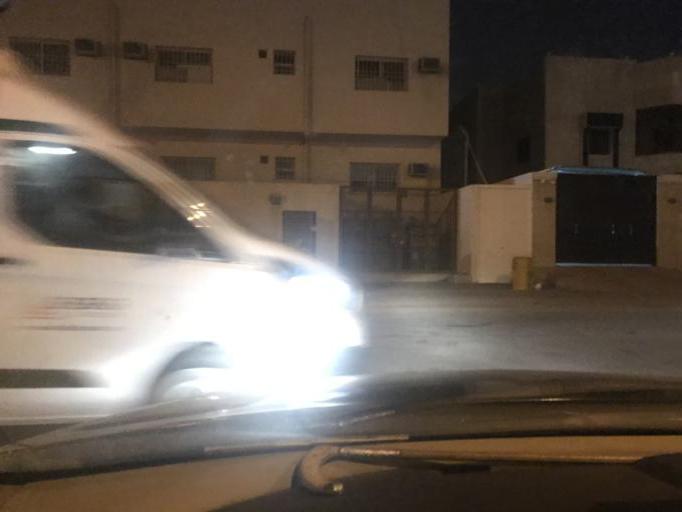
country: SA
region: Ar Riyad
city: Riyadh
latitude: 24.7505
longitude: 46.7746
